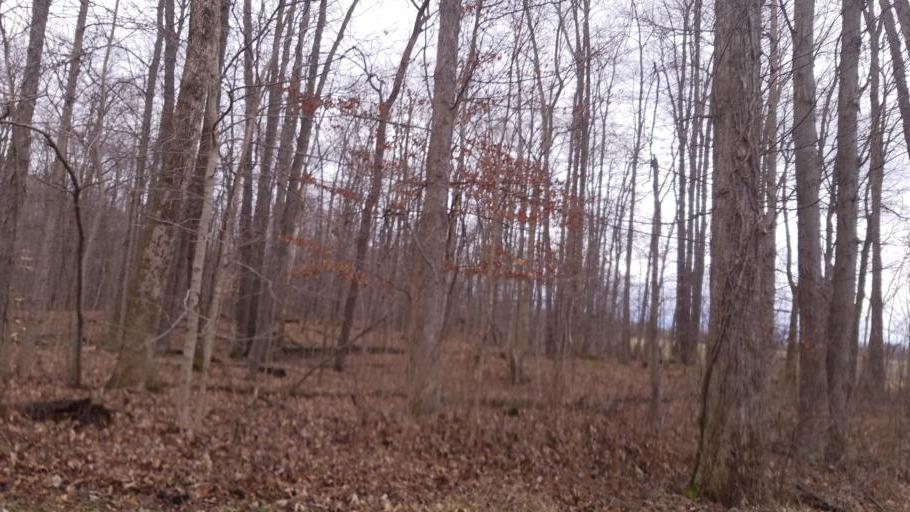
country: US
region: Ohio
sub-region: Knox County
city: Centerburg
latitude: 40.3423
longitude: -82.6084
